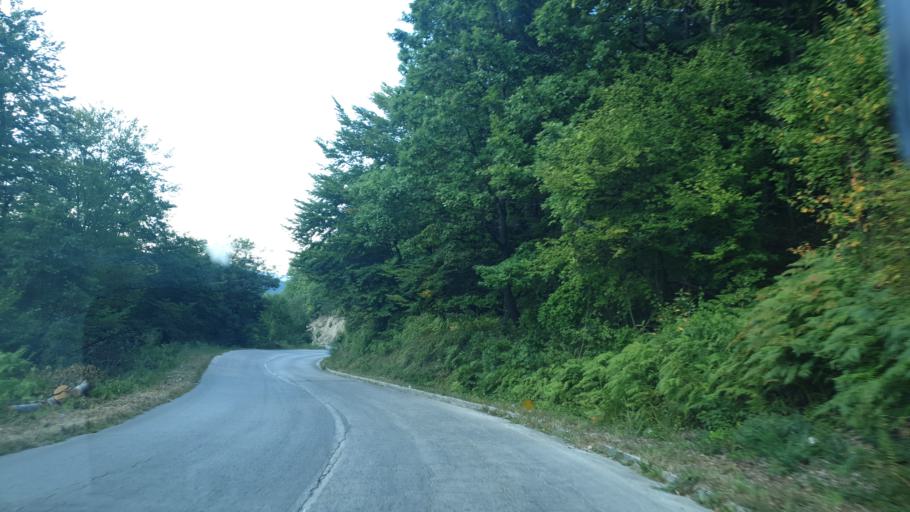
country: RS
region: Central Serbia
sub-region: Zlatiborski Okrug
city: Uzice
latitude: 43.8659
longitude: 19.9061
